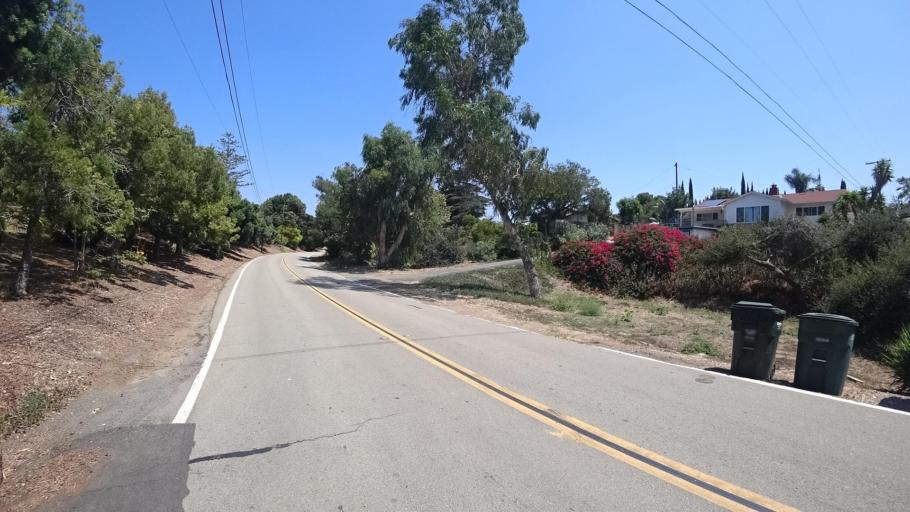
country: US
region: California
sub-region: San Diego County
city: Vista
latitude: 33.1838
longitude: -117.2641
